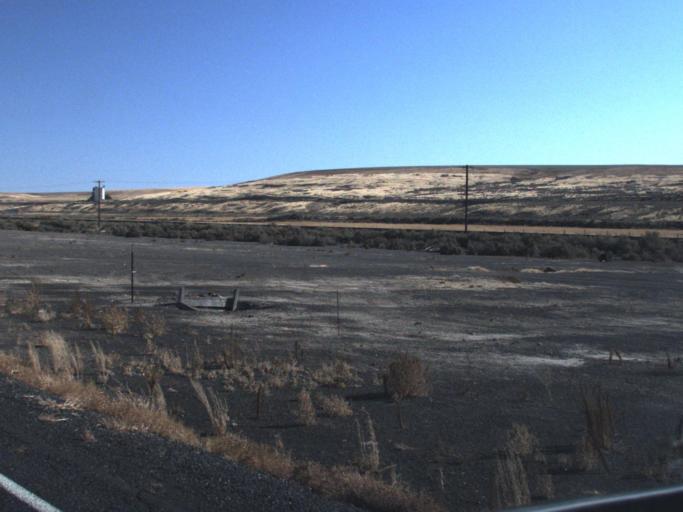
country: US
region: Washington
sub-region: Adams County
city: Ritzville
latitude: 46.9708
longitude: -118.5984
